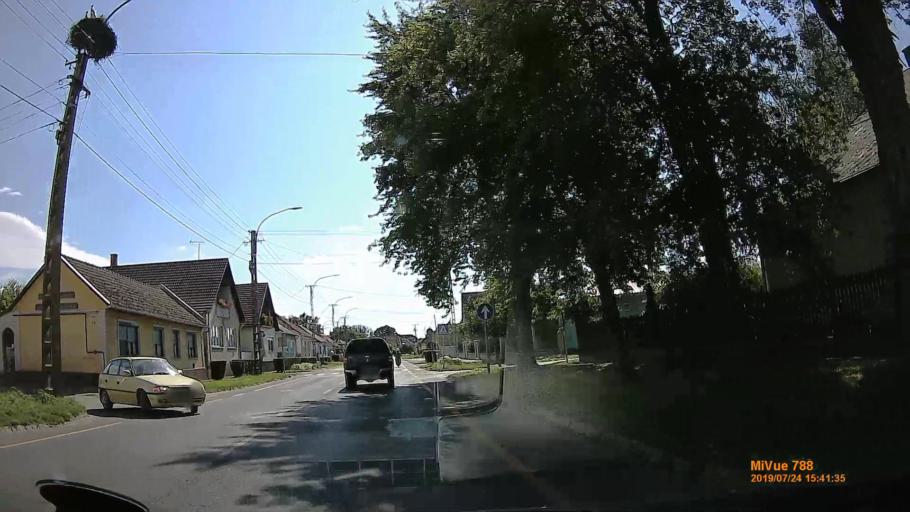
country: HU
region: Szabolcs-Szatmar-Bereg
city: Vasarosnameny
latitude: 48.1223
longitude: 22.3166
